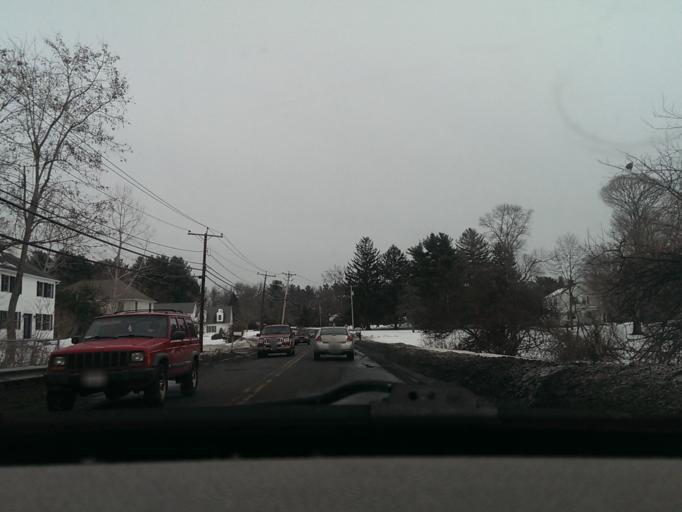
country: US
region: Massachusetts
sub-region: Hampden County
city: East Longmeadow
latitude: 42.0758
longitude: -72.4945
